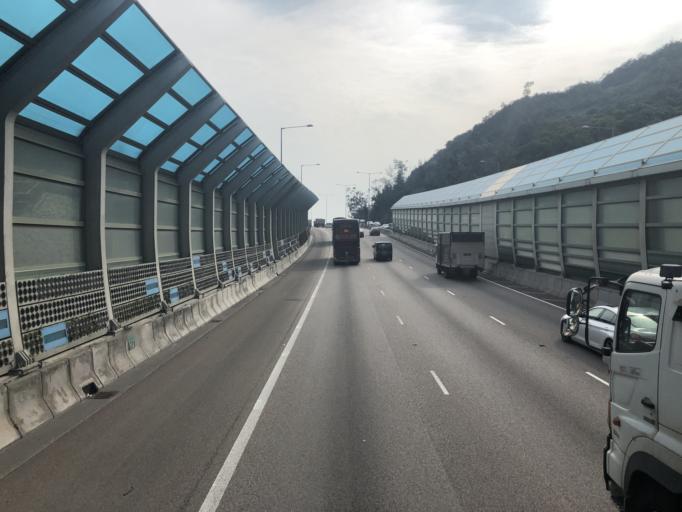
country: HK
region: Tsuen Wan
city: Tsuen Wan
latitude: 22.3624
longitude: 114.0390
